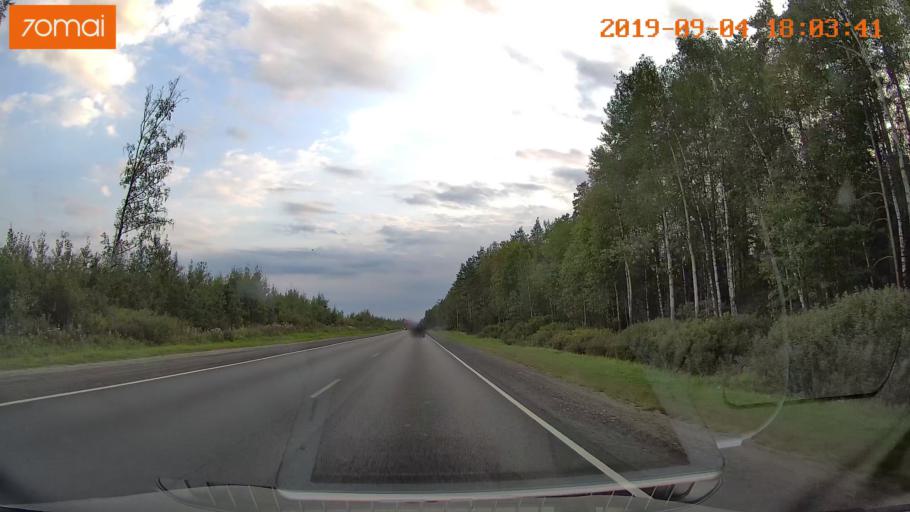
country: RU
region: Moskovskaya
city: Il'inskiy Pogost
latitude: 55.4606
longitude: 38.8489
